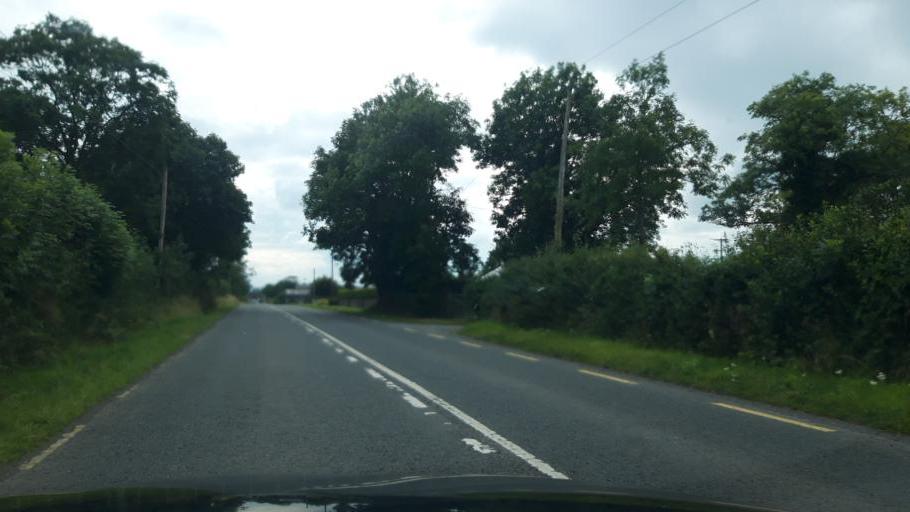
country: IE
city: Ballylinan
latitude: 52.8698
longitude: -7.0980
